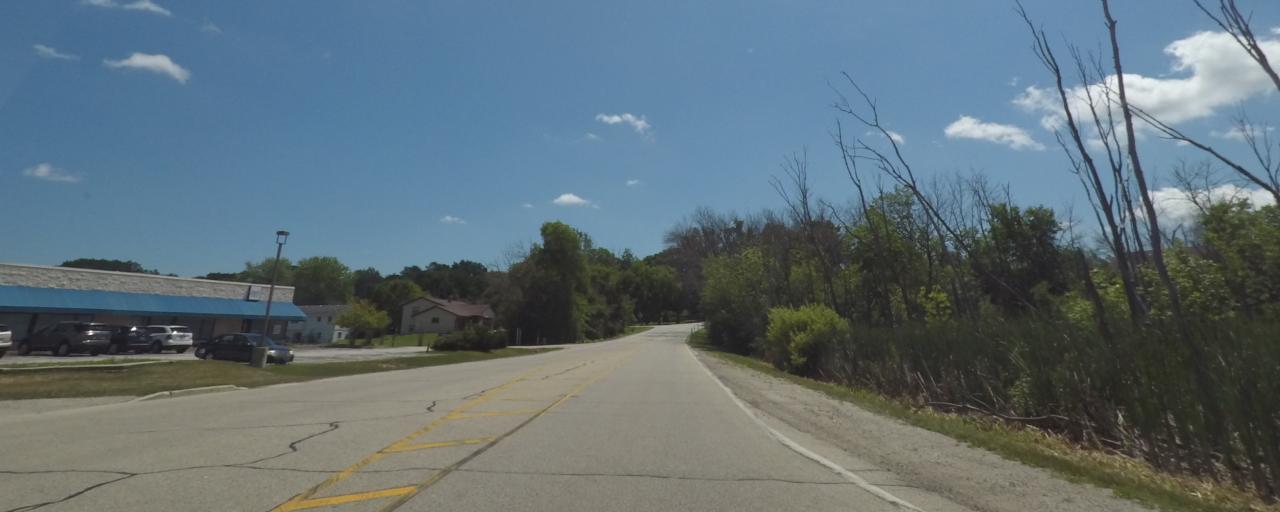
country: US
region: Wisconsin
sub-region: Waukesha County
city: Waukesha
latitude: 43.0488
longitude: -88.1853
